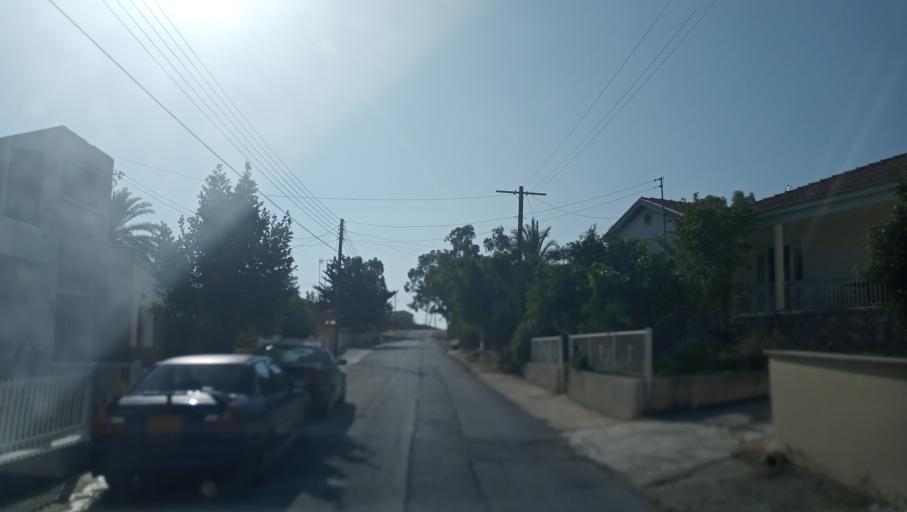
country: CY
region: Lefkosia
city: Geri
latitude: 35.1049
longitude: 33.4251
